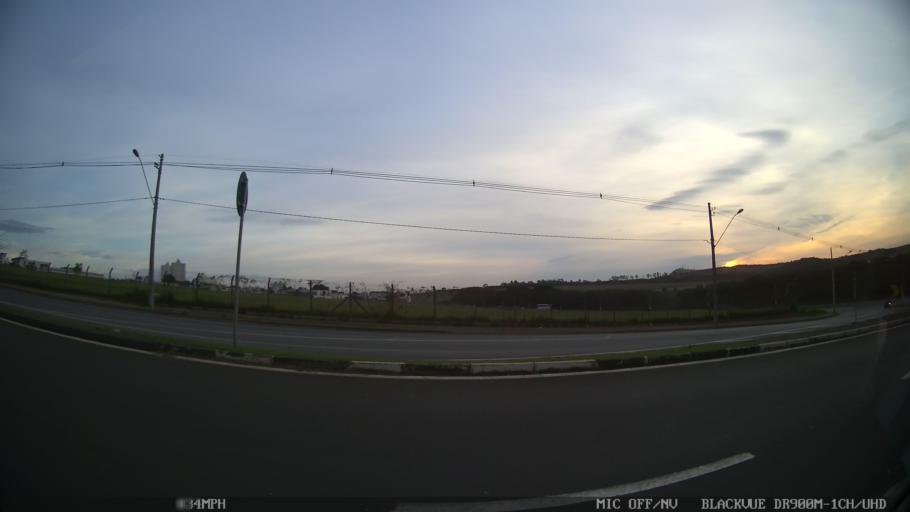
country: BR
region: Sao Paulo
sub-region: Limeira
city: Limeira
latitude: -22.5497
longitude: -47.4276
